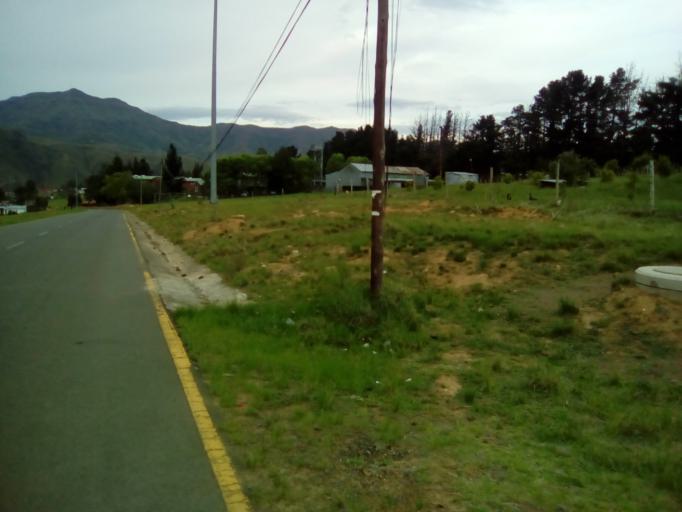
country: LS
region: Qacha's Nek
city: Qacha's Nek
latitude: -30.1138
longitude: 28.6805
